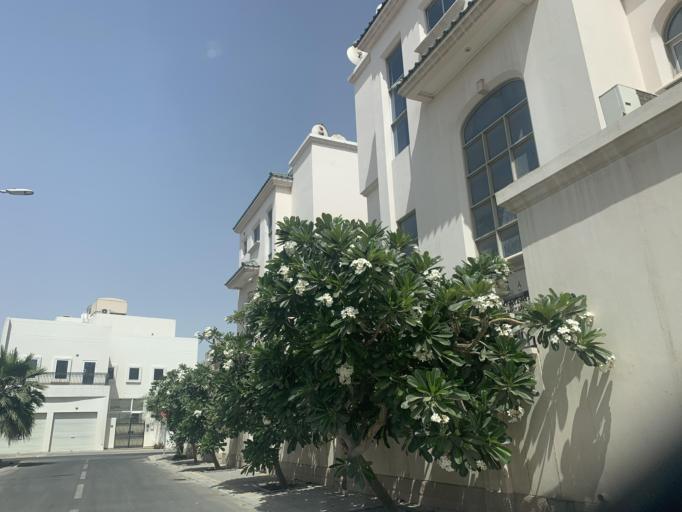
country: BH
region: Manama
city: Jidd Hafs
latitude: 26.2059
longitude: 50.5643
